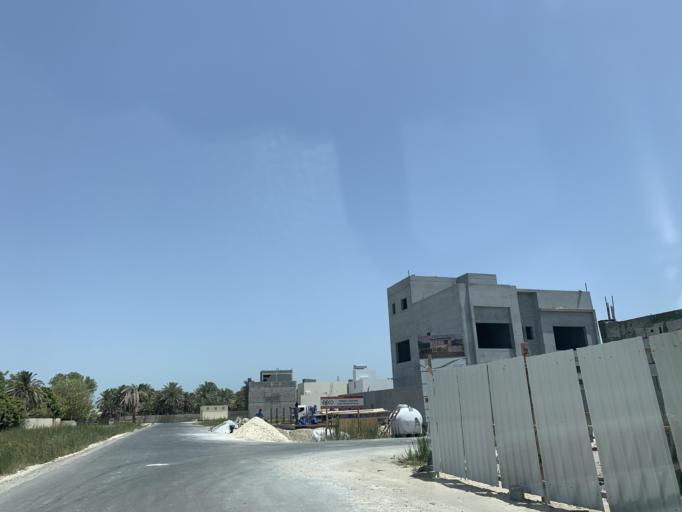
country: BH
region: Manama
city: Jidd Hafs
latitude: 26.2250
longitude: 50.4710
